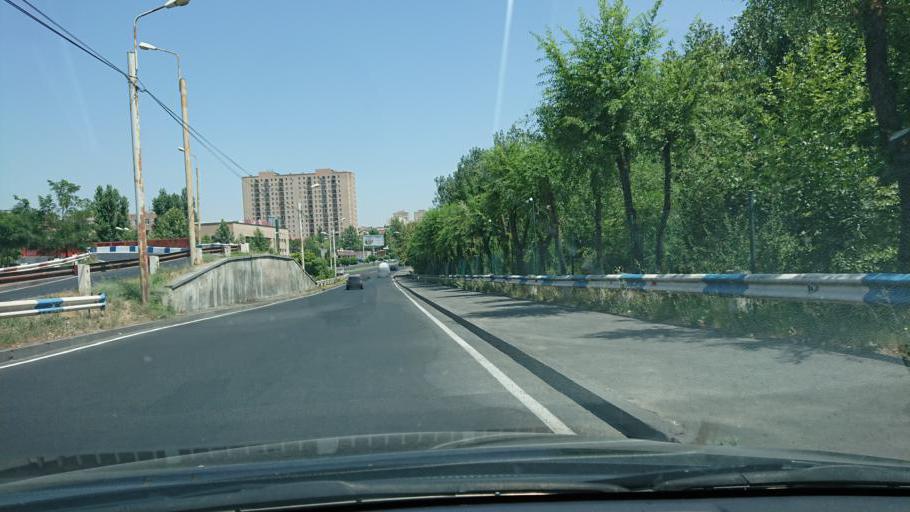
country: AM
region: Yerevan
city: Yerevan
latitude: 40.2129
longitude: 44.4921
